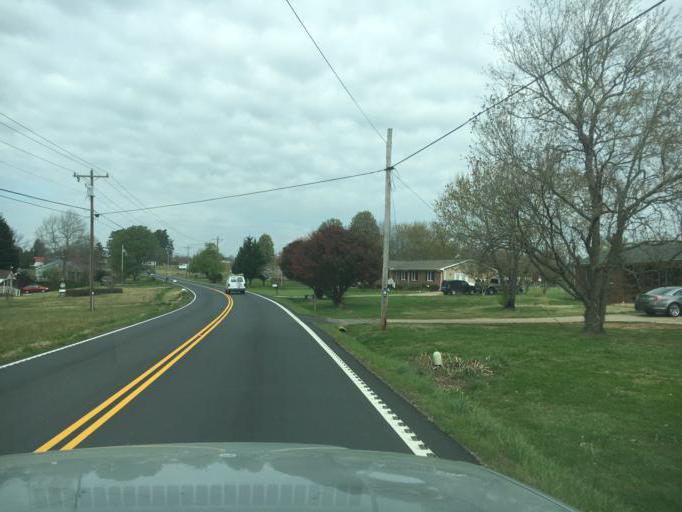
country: US
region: South Carolina
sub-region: Spartanburg County
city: Inman Mills
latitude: 35.0572
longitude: -82.1481
